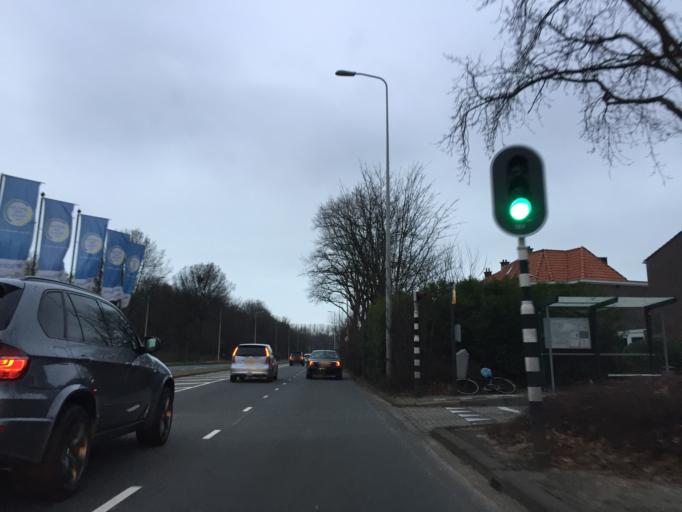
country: NL
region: South Holland
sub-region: Gemeente Westland
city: Poeldijk
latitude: 52.0522
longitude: 4.2293
